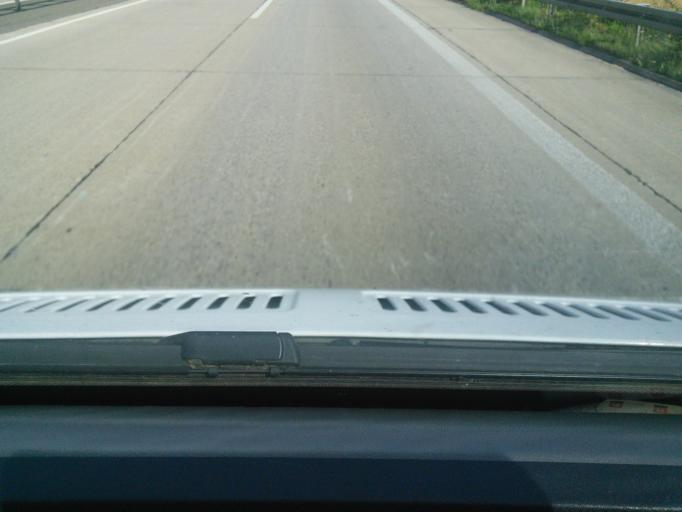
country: DE
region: North Rhine-Westphalia
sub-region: Regierungsbezirk Dusseldorf
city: Viersen
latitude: 51.2104
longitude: 6.3652
